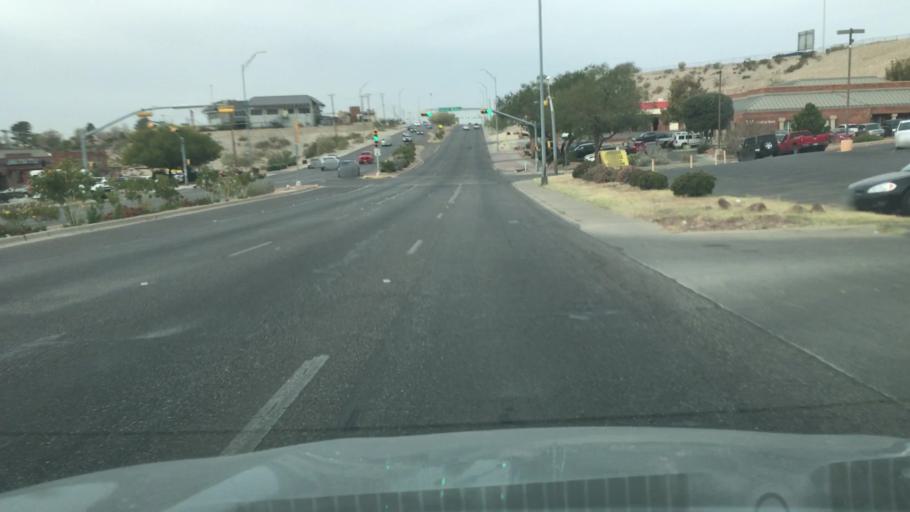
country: US
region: New Mexico
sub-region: Dona Ana County
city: Sunland Park
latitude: 31.8341
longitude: -106.5416
